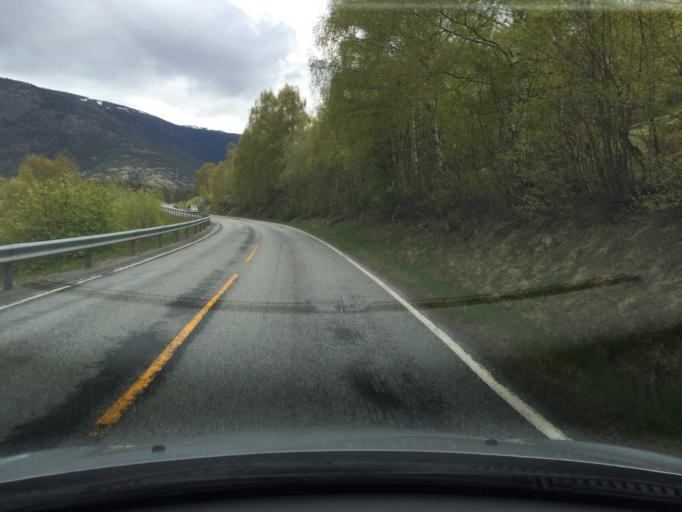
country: NO
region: Oppland
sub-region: Lom
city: Fossbergom
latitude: 61.8285
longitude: 8.5497
